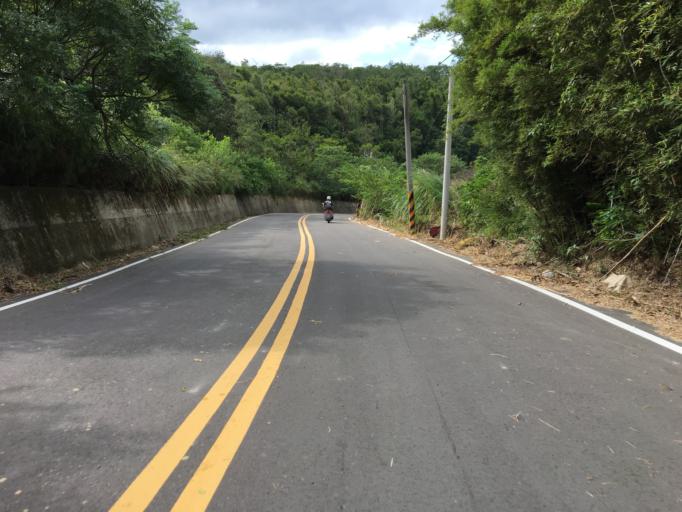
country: TW
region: Taiwan
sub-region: Hsinchu
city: Hsinchu
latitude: 24.7063
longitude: 120.9532
